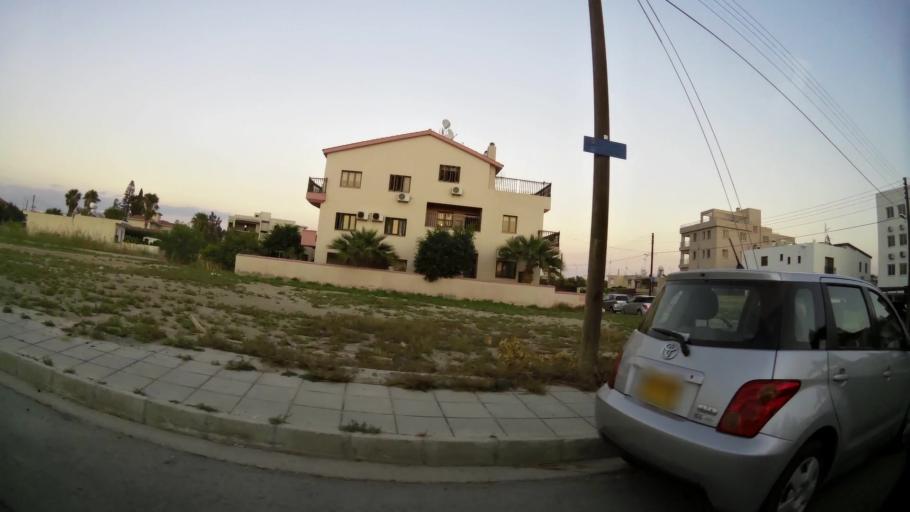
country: CY
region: Larnaka
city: Larnaca
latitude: 34.9137
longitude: 33.5972
